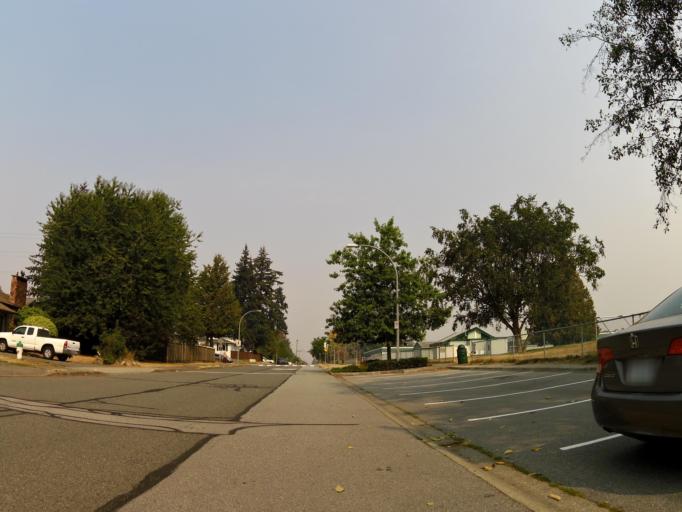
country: CA
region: British Columbia
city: Delta
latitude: 49.1502
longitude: -122.9238
